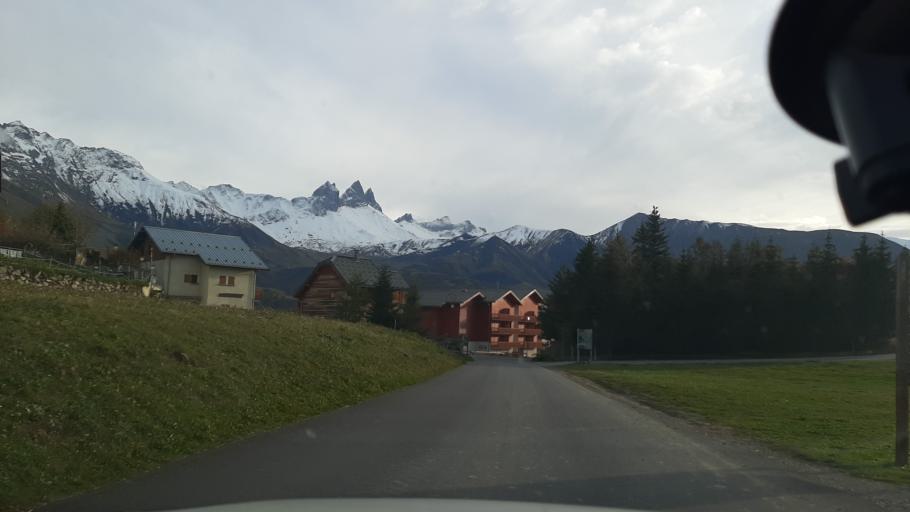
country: FR
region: Rhone-Alpes
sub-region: Departement de la Savoie
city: Villargondran
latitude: 45.2104
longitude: 6.3371
